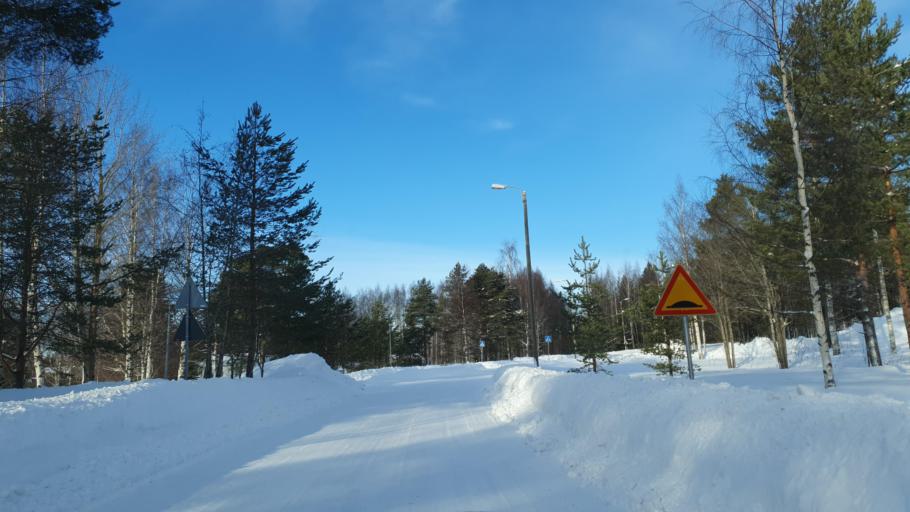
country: FI
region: Northern Ostrobothnia
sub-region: Oulu
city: Haukipudas
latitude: 65.1938
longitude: 25.4123
